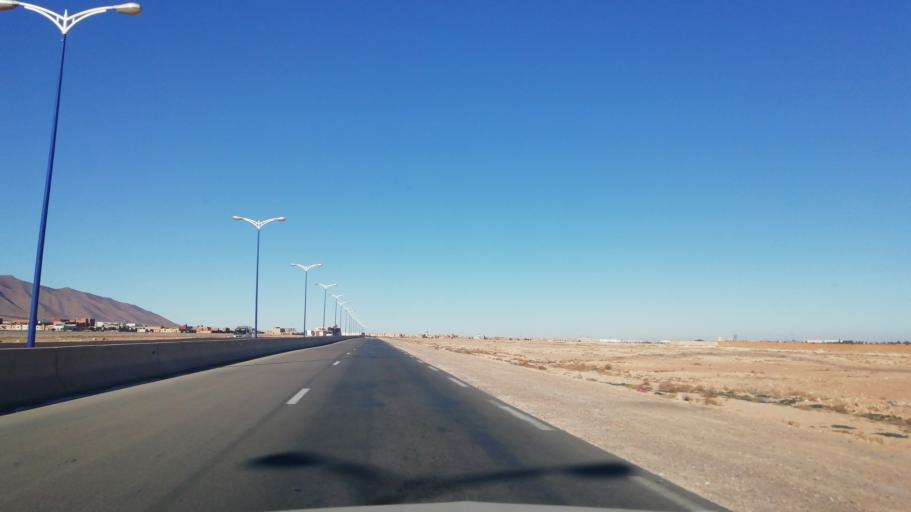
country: DZ
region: Wilaya de Naama
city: Naama
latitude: 33.5227
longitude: -0.2751
